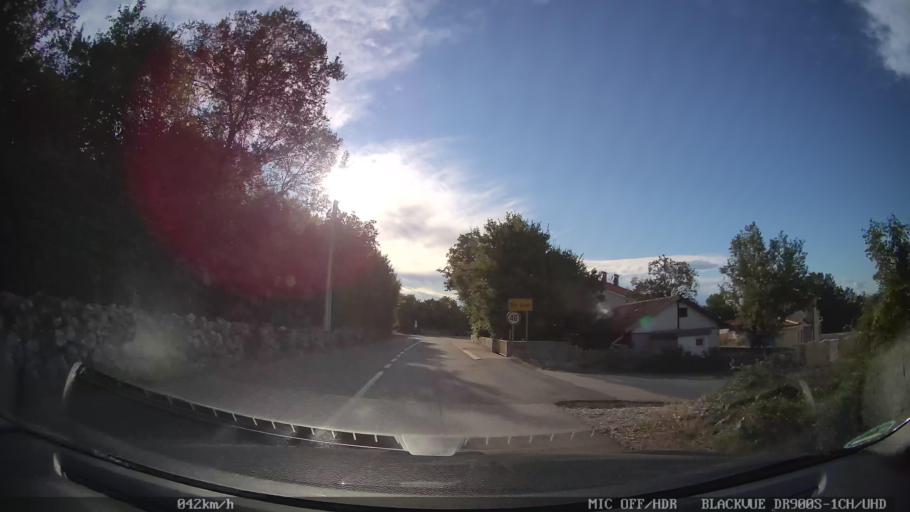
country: HR
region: Primorsko-Goranska
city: Njivice
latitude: 45.0989
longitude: 14.5308
